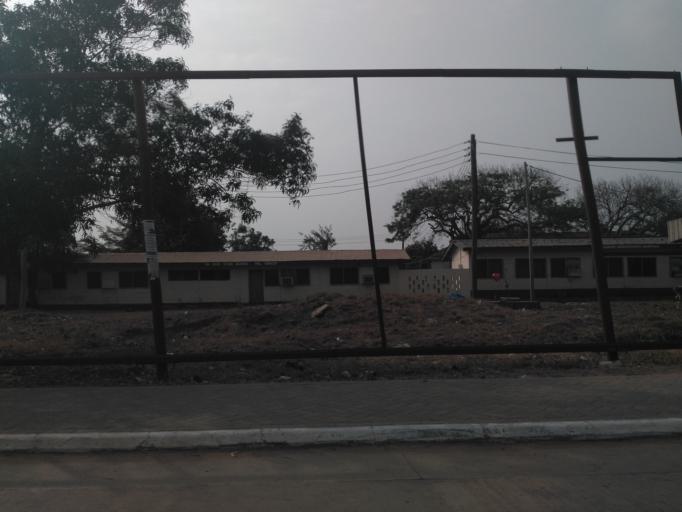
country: GH
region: Greater Accra
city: Accra
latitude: 5.5484
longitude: -0.1957
